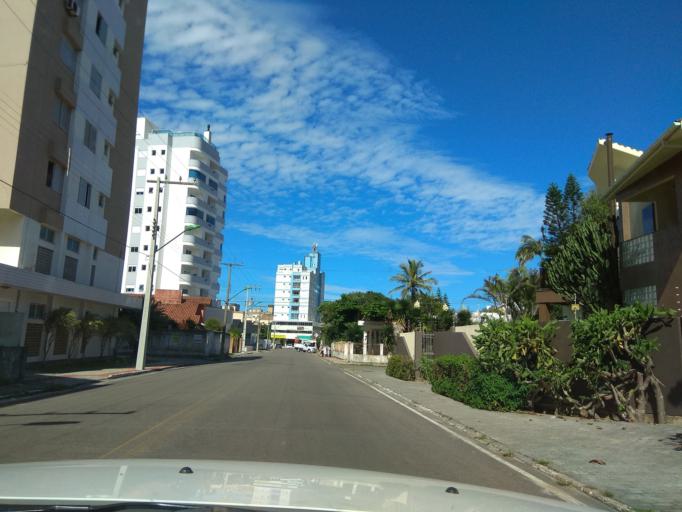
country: BR
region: Santa Catarina
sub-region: Laguna
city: Laguna
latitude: -28.4789
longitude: -48.7707
